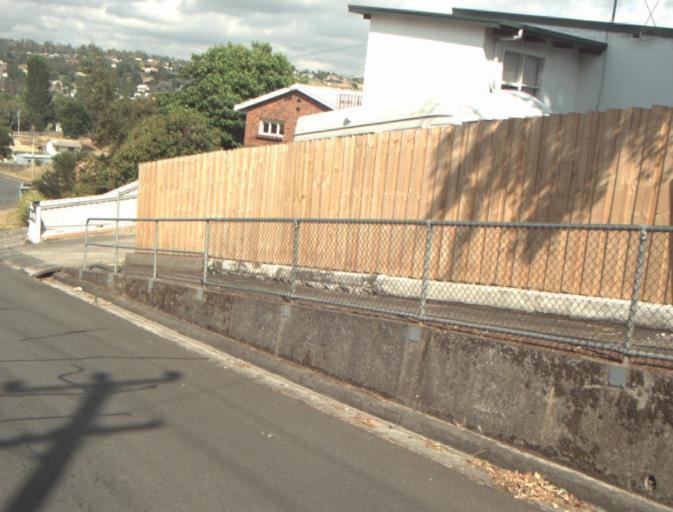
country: AU
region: Tasmania
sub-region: Launceston
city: Newstead
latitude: -41.4614
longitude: 147.1964
